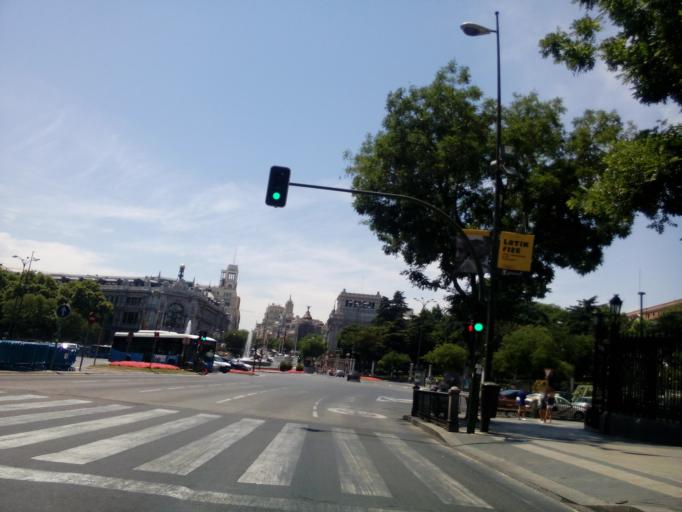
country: ES
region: Madrid
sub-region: Provincia de Madrid
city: Retiro
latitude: 40.4196
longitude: -3.6912
